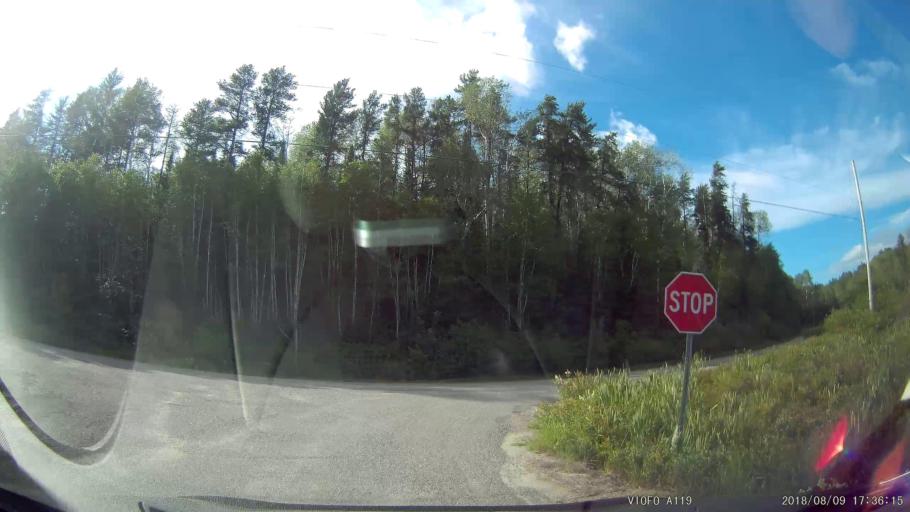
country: CA
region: Ontario
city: Rayside-Balfour
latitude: 46.6165
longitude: -81.4659
